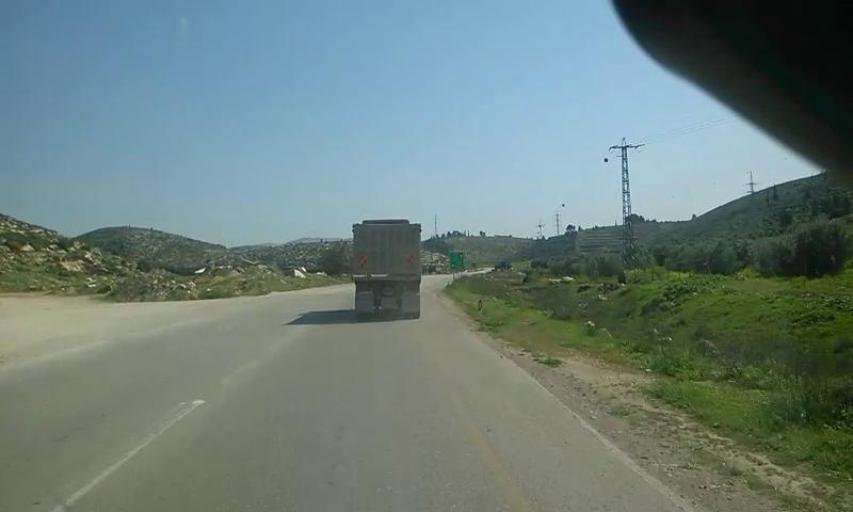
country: PS
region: West Bank
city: Idhna
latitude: 31.5858
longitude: 34.9729
